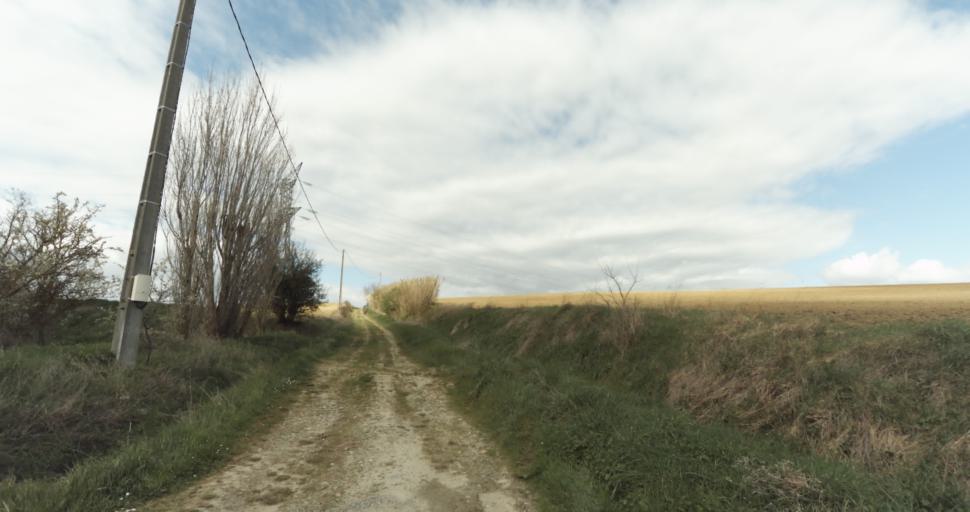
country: FR
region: Midi-Pyrenees
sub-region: Departement de la Haute-Garonne
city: Auterive
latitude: 43.3886
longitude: 1.4718
